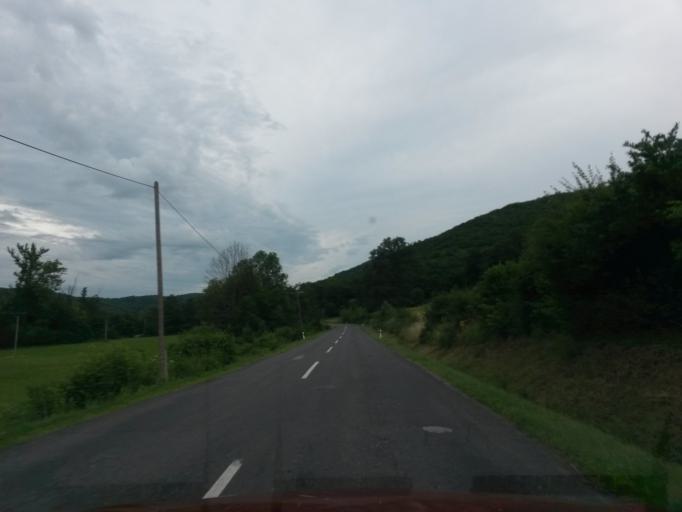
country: SK
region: Banskobystricky
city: Velky Krtis
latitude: 48.3453
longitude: 19.4081
